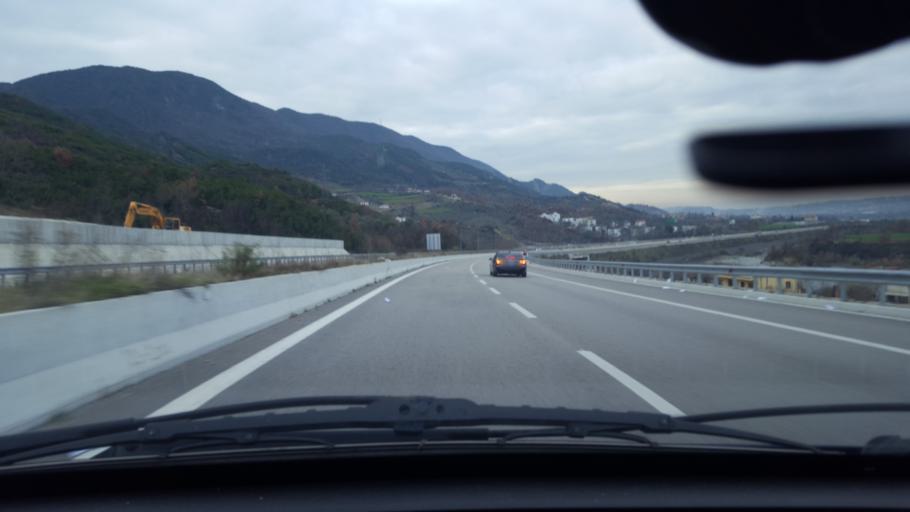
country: AL
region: Tirane
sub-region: Rrethi i Tiranes
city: Berzhite
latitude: 41.2338
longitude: 19.9228
